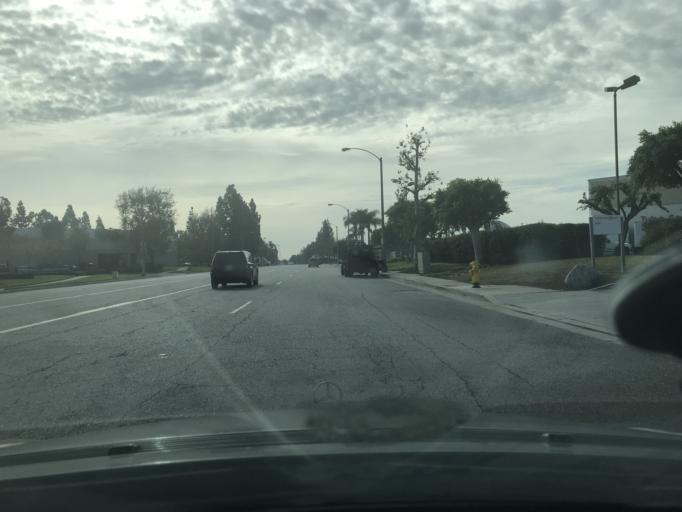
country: US
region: California
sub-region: Los Angeles County
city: Santa Fe Springs
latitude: 33.9566
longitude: -118.0717
